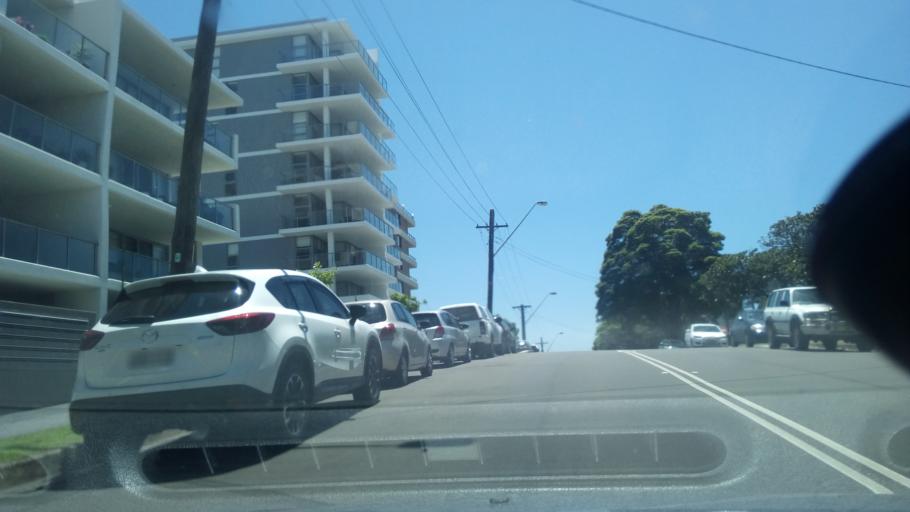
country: AU
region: New South Wales
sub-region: Wollongong
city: Wollongong
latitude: -34.4177
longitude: 150.8970
